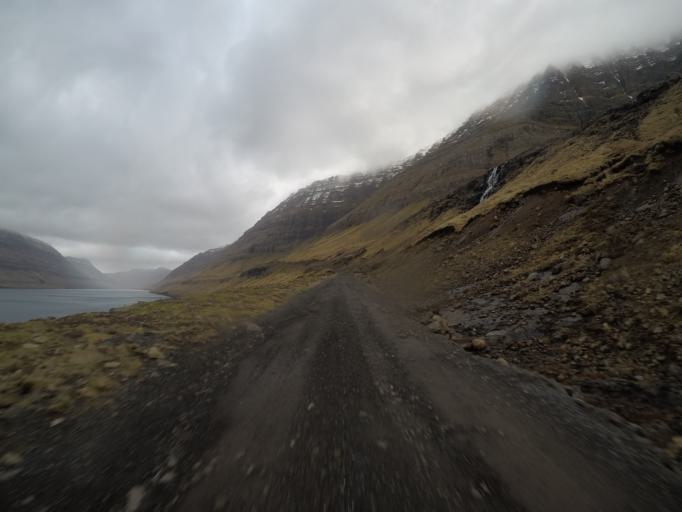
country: FO
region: Nordoyar
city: Klaksvik
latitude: 62.3428
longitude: -6.5801
